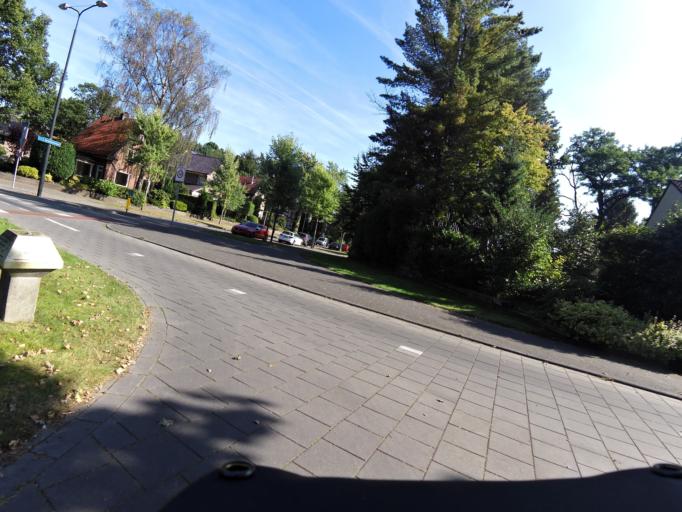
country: NL
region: Gelderland
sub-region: Gemeente Apeldoorn
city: Apeldoorn
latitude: 52.2072
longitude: 5.9304
